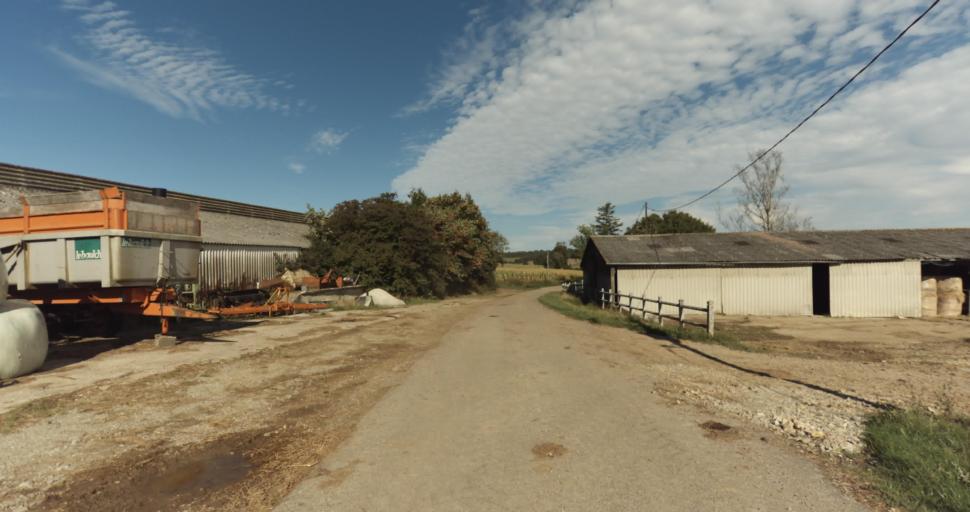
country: FR
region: Lower Normandy
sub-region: Departement de l'Orne
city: Gace
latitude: 48.8049
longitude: 0.2279
